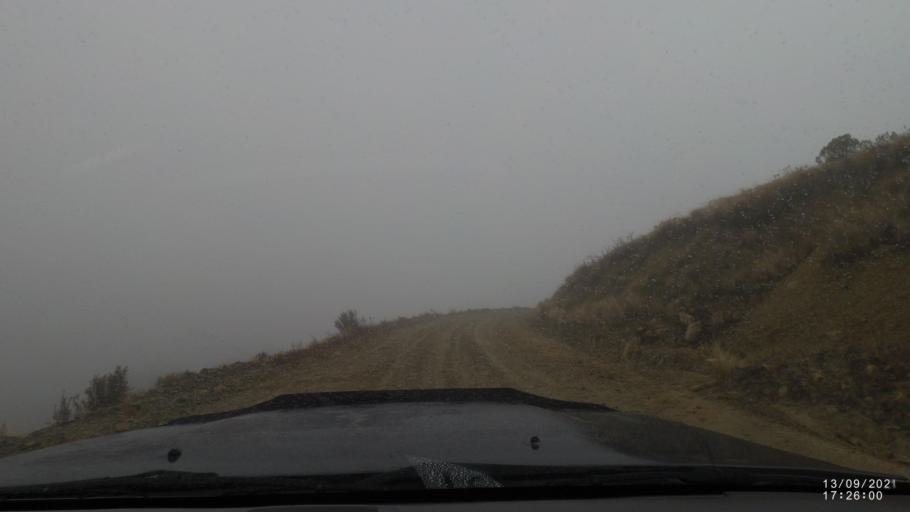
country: BO
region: Cochabamba
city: Colomi
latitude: -17.3609
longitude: -65.7827
